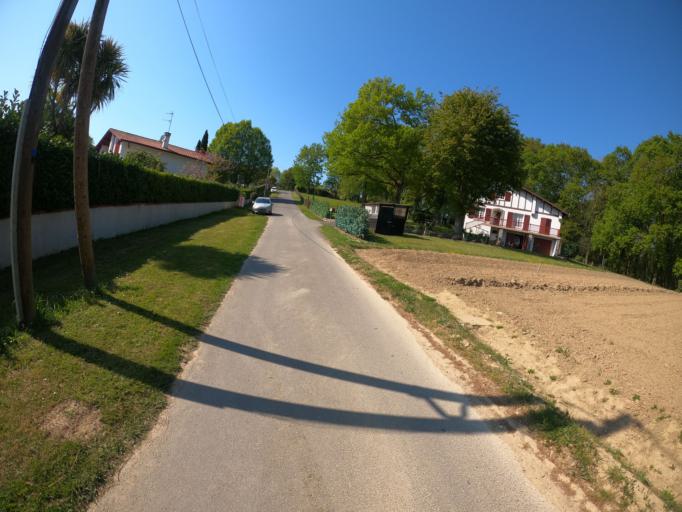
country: FR
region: Aquitaine
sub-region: Departement des Pyrenees-Atlantiques
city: Bassussarry
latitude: 43.4369
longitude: -1.4992
